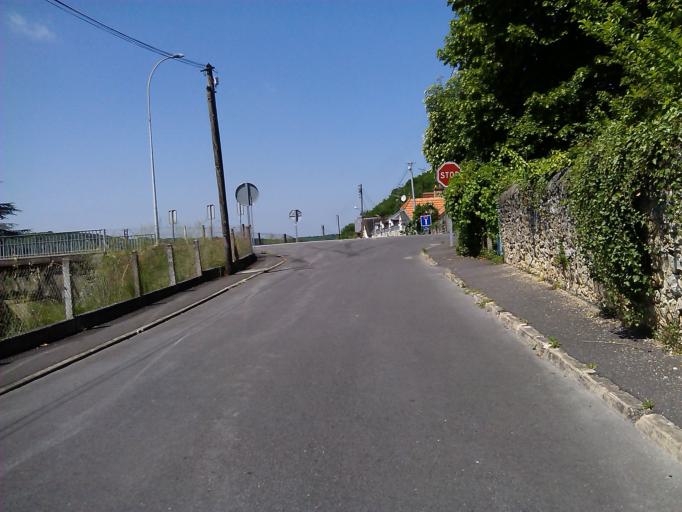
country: FR
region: Centre
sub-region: Departement de l'Indre
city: Saint-Marcel
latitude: 46.5970
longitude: 1.5118
